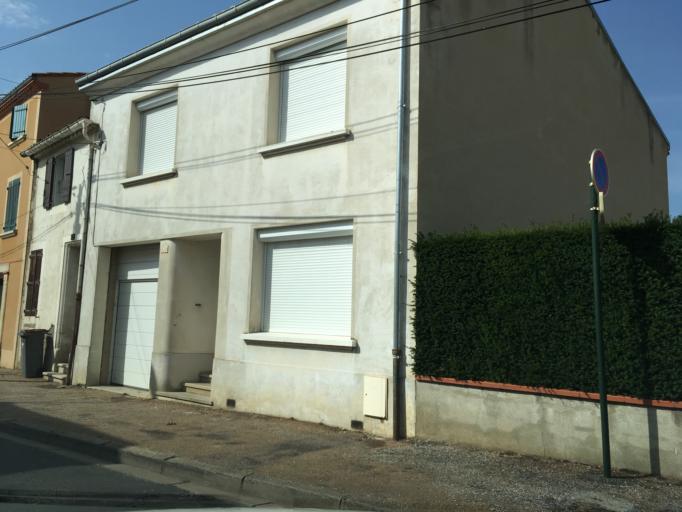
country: FR
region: Midi-Pyrenees
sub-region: Departement du Tarn
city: Castres
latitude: 43.6037
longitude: 2.2523
